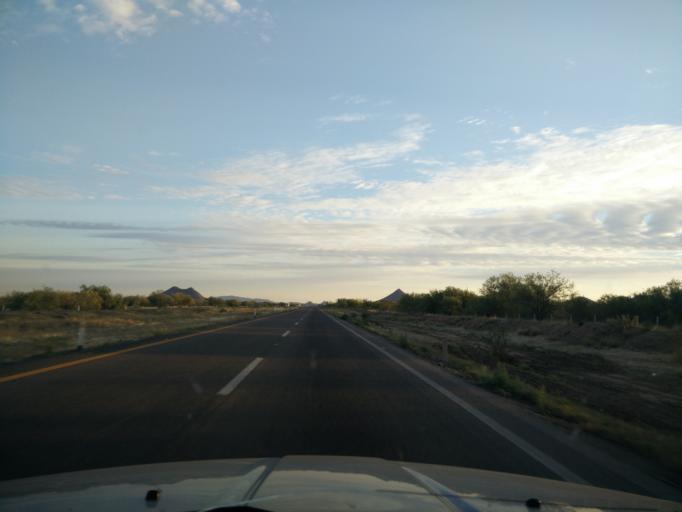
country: MX
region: Sonora
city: Hermosillo
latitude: 28.7616
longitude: -110.9697
